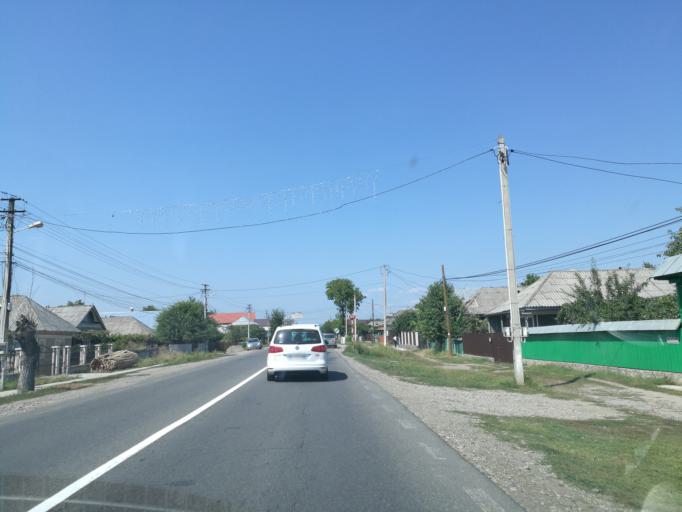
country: RO
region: Neamt
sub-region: Comuna Roznov
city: Chintinici
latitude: 46.8414
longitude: 26.5017
